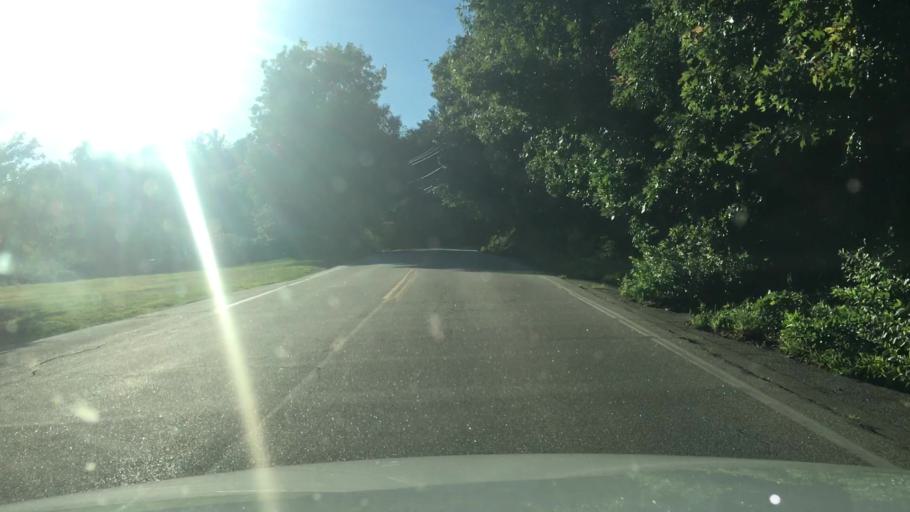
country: US
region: New Hampshire
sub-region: Rockingham County
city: Sandown
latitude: 42.9167
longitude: -71.1660
